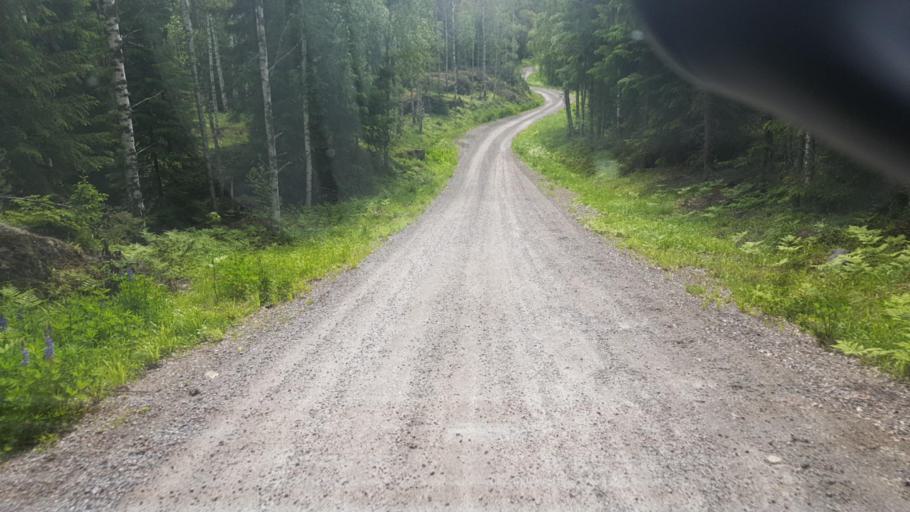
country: SE
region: Vaermland
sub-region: Eda Kommun
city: Amotfors
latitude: 59.8267
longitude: 12.4025
